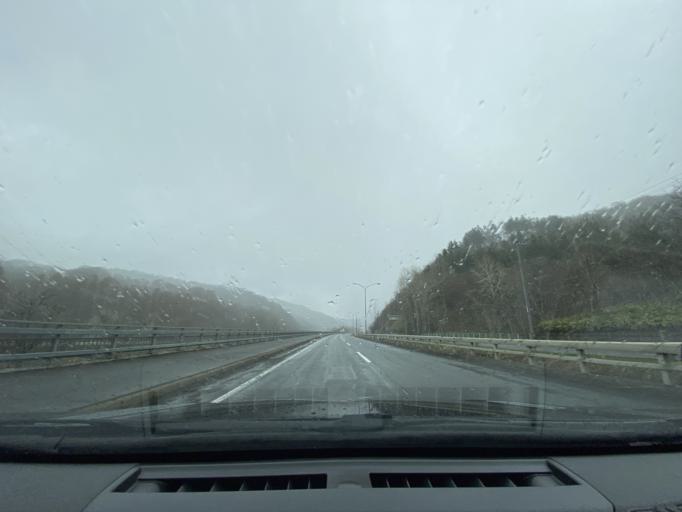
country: JP
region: Hokkaido
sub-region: Asahikawa-shi
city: Asahikawa
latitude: 43.7274
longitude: 142.2198
